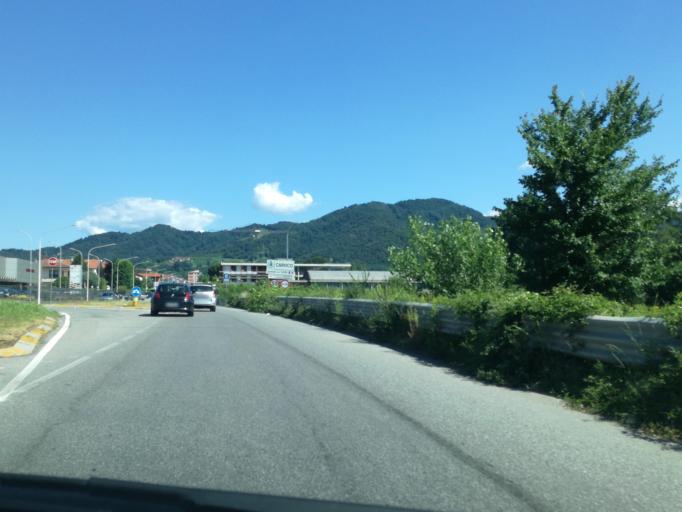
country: IT
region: Lombardy
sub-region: Provincia di Bergamo
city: Carvico
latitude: 45.6946
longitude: 9.4812
